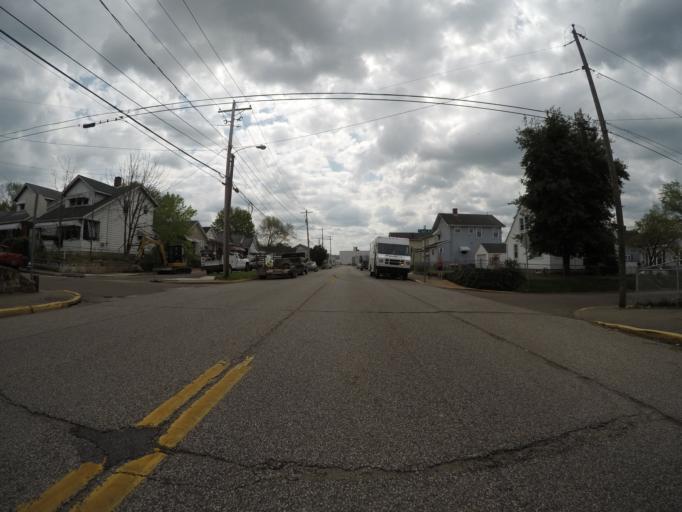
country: US
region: West Virginia
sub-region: Kanawha County
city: Charleston
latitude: 38.3684
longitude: -81.6560
